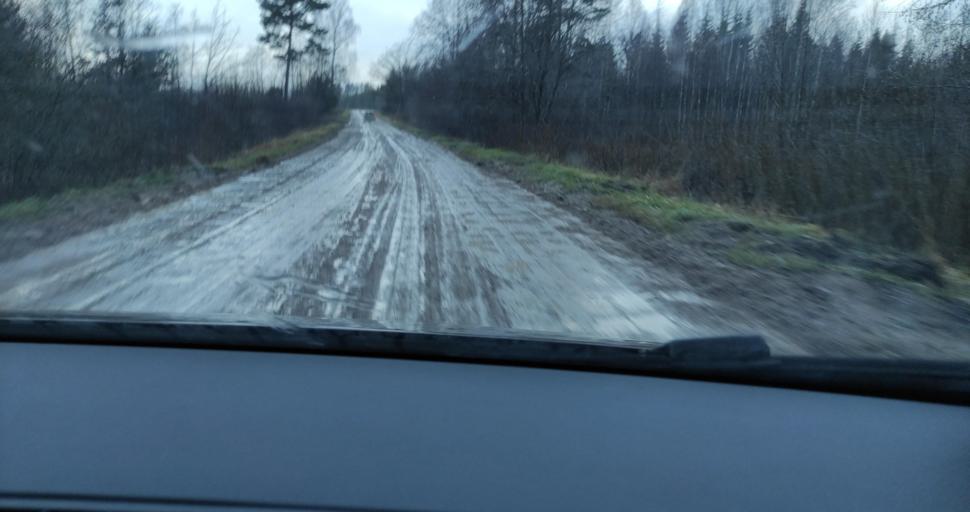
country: LV
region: Skrunda
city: Skrunda
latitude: 56.7073
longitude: 22.2083
